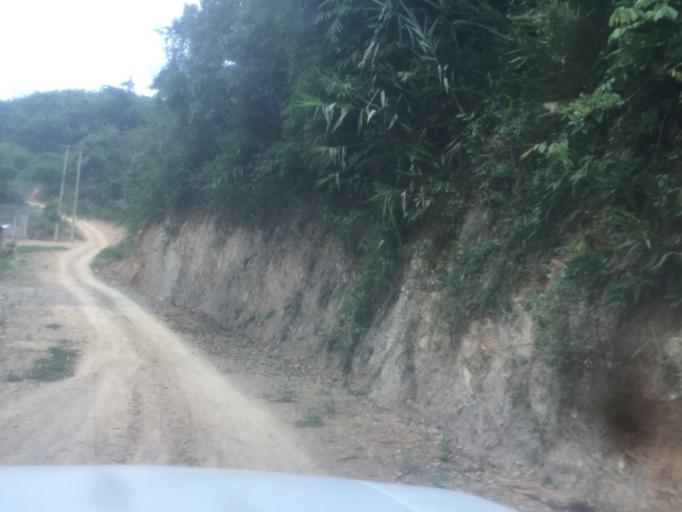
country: LA
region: Phongsali
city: Khoa
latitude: 20.9119
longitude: 102.5601
